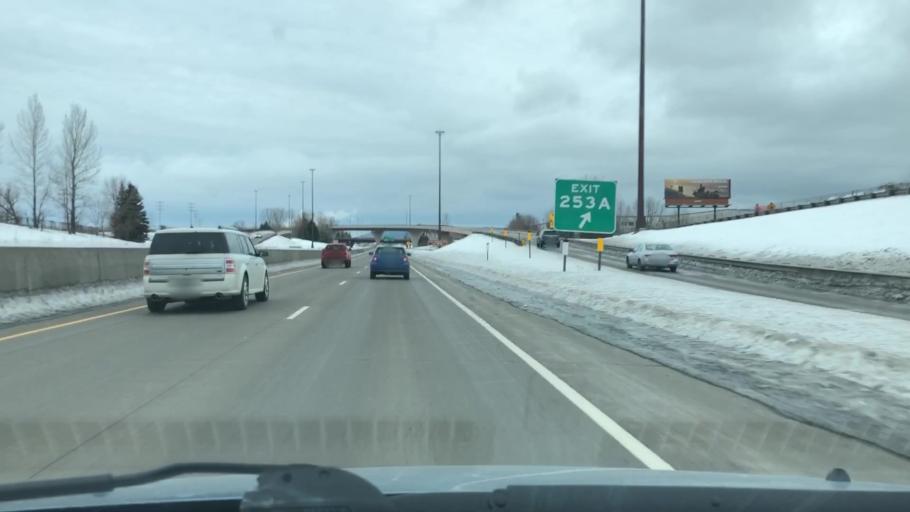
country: US
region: Wisconsin
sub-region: Douglas County
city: Superior
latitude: 46.7470
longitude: -92.1489
